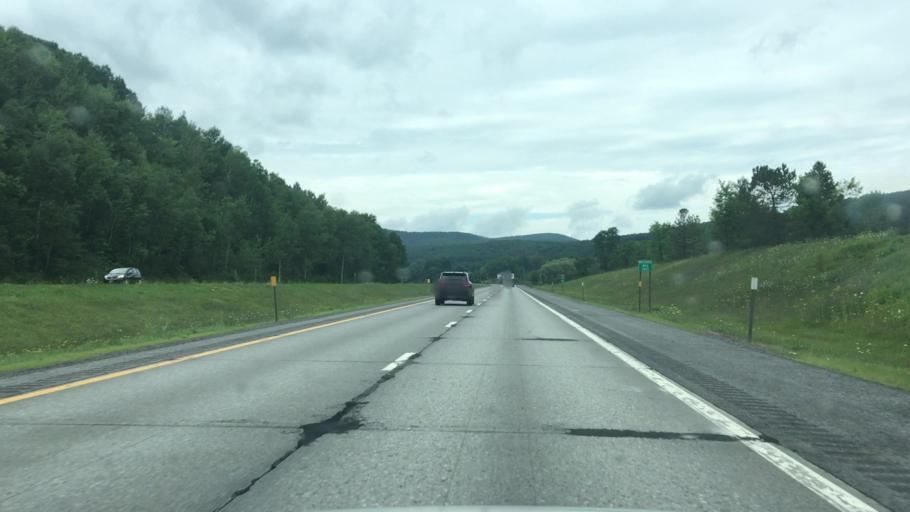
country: US
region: New York
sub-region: Schoharie County
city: Cobleskill
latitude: 42.6463
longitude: -74.5929
